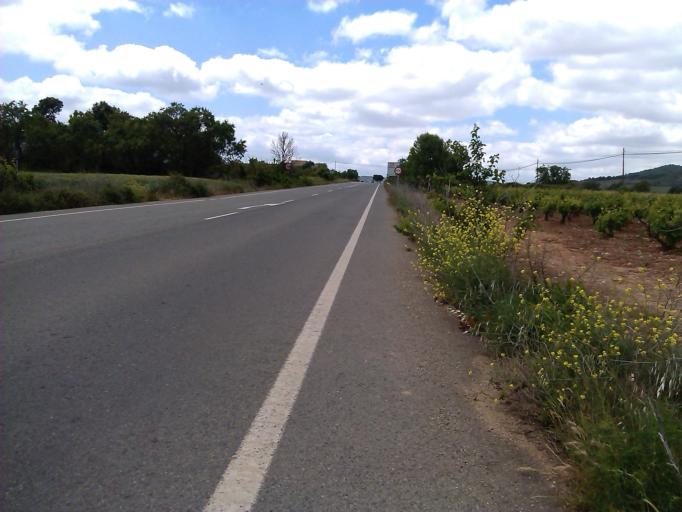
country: ES
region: La Rioja
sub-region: Provincia de La Rioja
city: Navarrete
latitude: 42.4222
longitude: -2.5860
